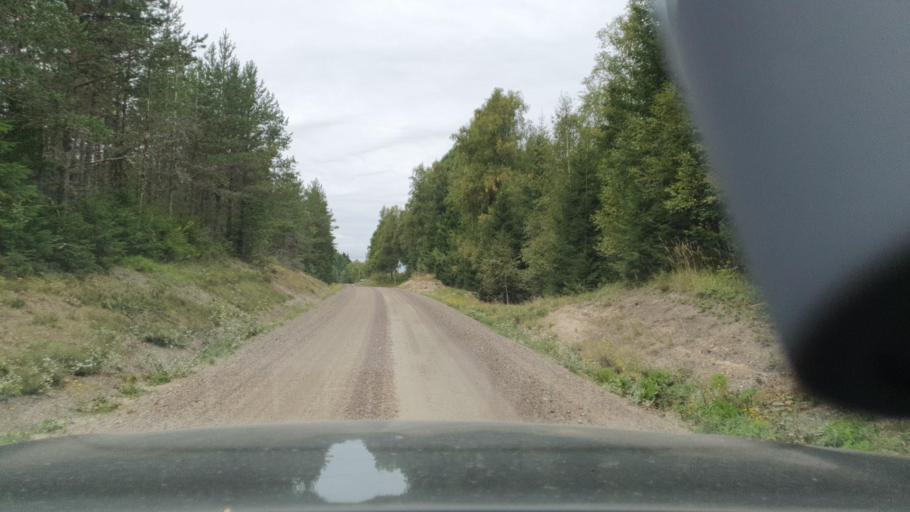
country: SE
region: Vaermland
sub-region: Eda Kommun
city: Charlottenberg
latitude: 60.0569
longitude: 12.5575
